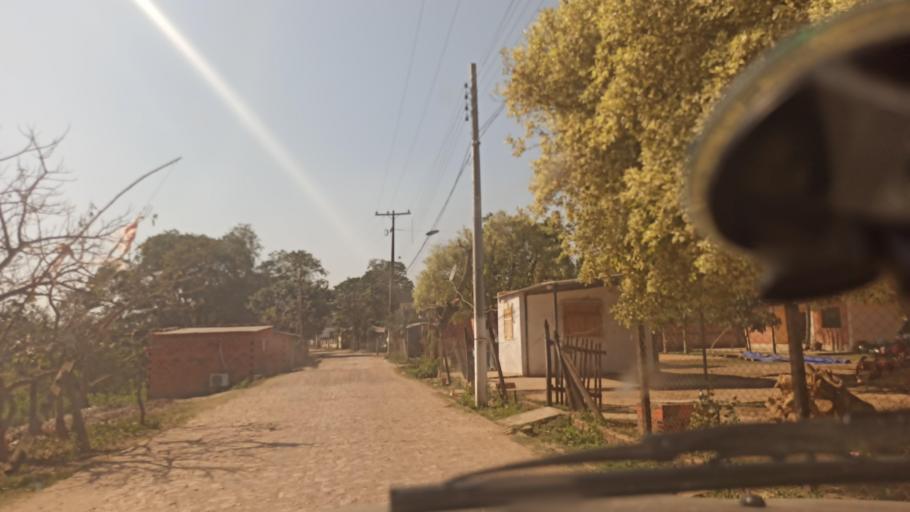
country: AR
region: Formosa
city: Clorinda
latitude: -25.2937
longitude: -57.6977
